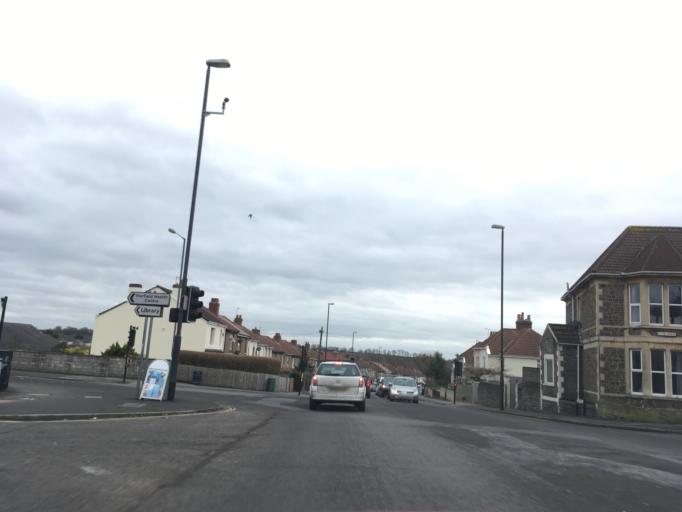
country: GB
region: England
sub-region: Bristol
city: Bristol
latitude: 51.4886
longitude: -2.5825
